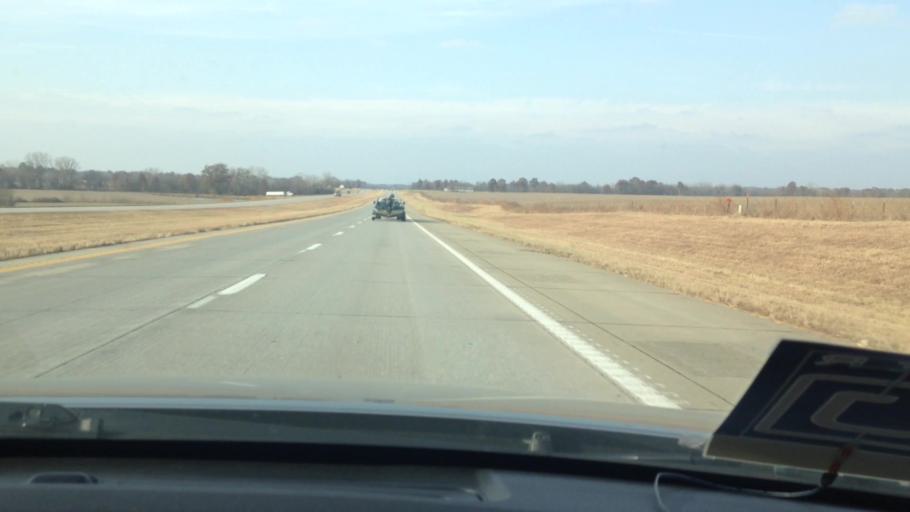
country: US
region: Missouri
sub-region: Henry County
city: Clinton
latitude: 38.4471
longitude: -93.9570
